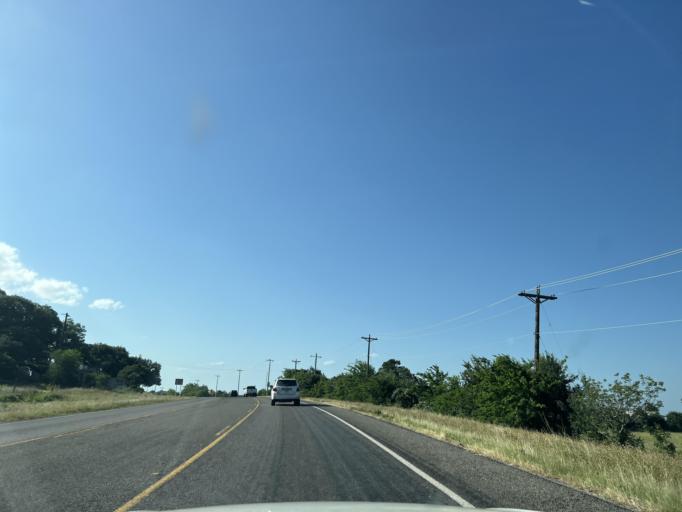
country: US
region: Texas
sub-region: Washington County
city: Brenham
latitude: 30.1739
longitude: -96.3818
